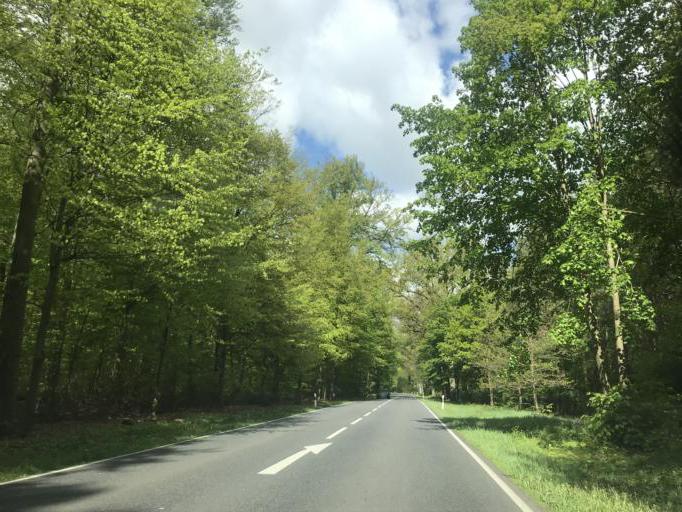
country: DE
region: Brandenburg
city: Marienwerder
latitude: 52.8636
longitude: 13.5191
